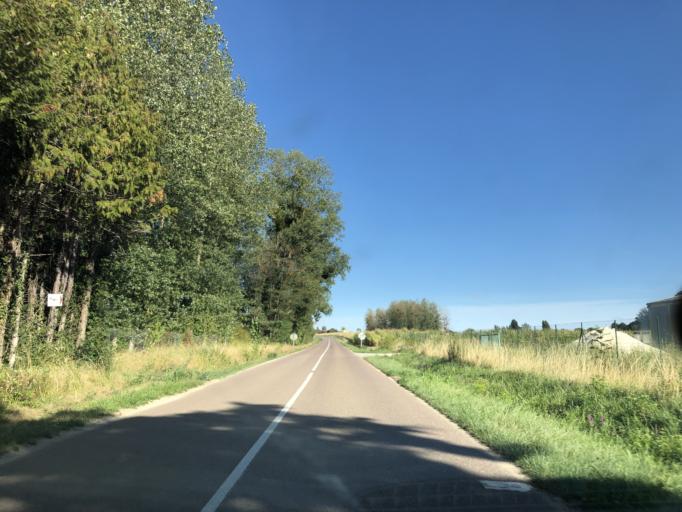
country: FR
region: Bourgogne
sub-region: Departement de l'Yonne
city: Seignelay
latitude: 47.9023
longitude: 3.6118
